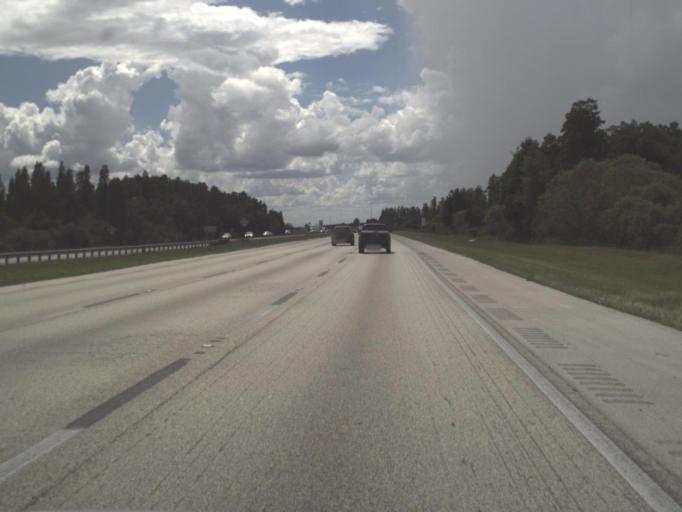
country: US
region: Florida
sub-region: Polk County
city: Polk City
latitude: 28.1791
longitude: -81.7520
